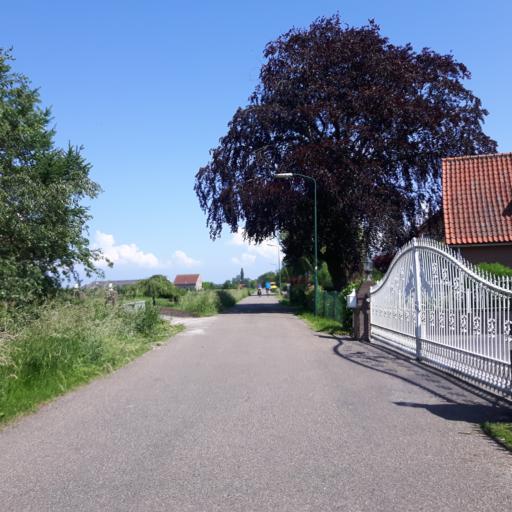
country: NL
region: Utrecht
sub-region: Gemeente Utrecht
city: Utrecht
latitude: 52.1402
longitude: 5.1182
